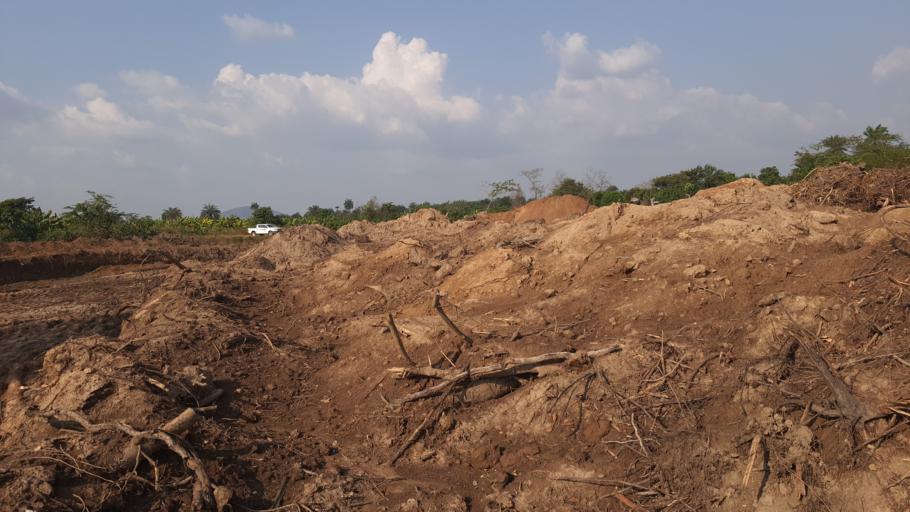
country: NG
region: Osun
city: Iwo
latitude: 7.7112
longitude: 4.1110
